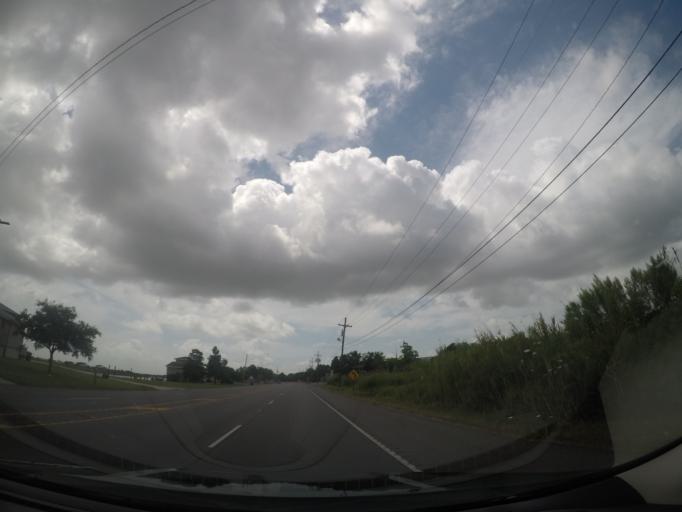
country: US
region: Louisiana
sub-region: Saint Tammany Parish
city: Eden Isle
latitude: 30.0711
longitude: -89.8384
